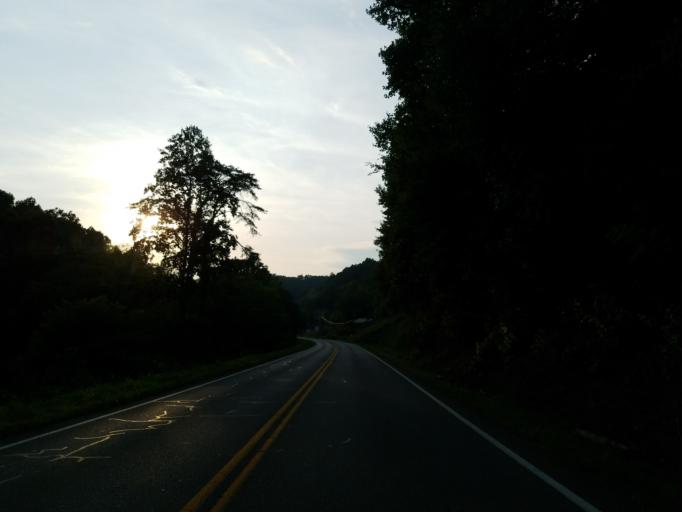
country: US
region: Georgia
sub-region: Gilmer County
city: Ellijay
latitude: 34.6852
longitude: -84.4596
